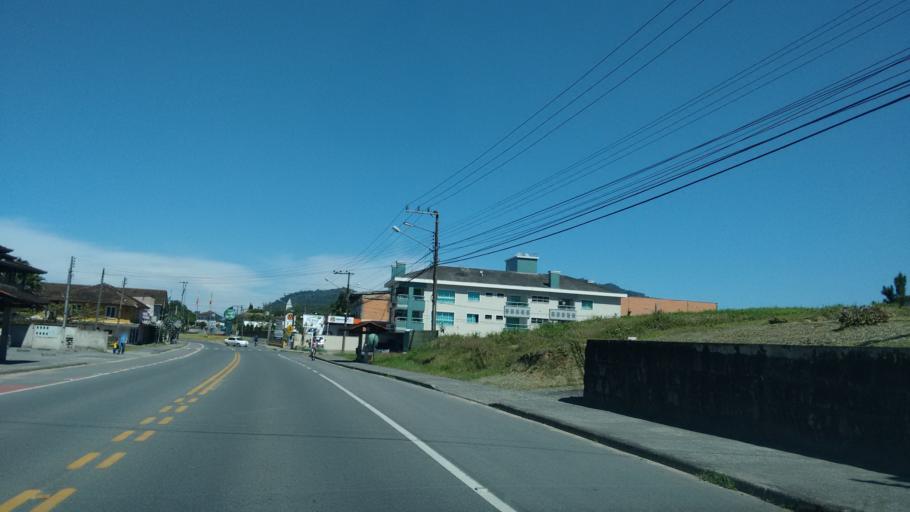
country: BR
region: Santa Catarina
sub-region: Pomerode
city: Pomerode
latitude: -26.7493
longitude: -49.1738
